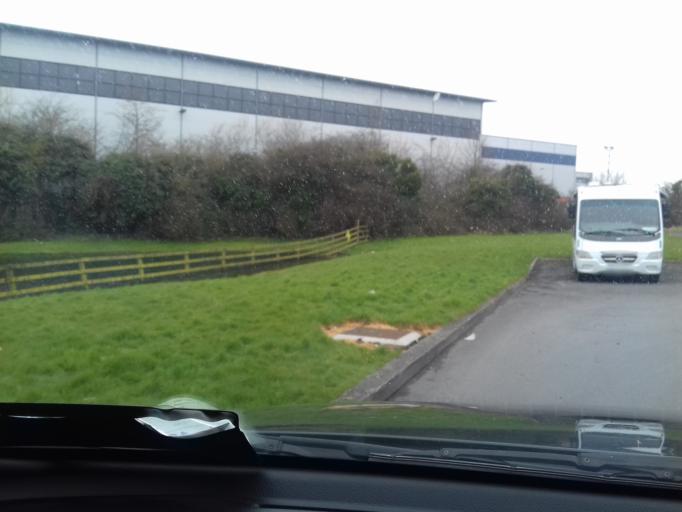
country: IE
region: Leinster
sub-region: Dublin City
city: Finglas
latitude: 53.3997
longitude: -6.3145
